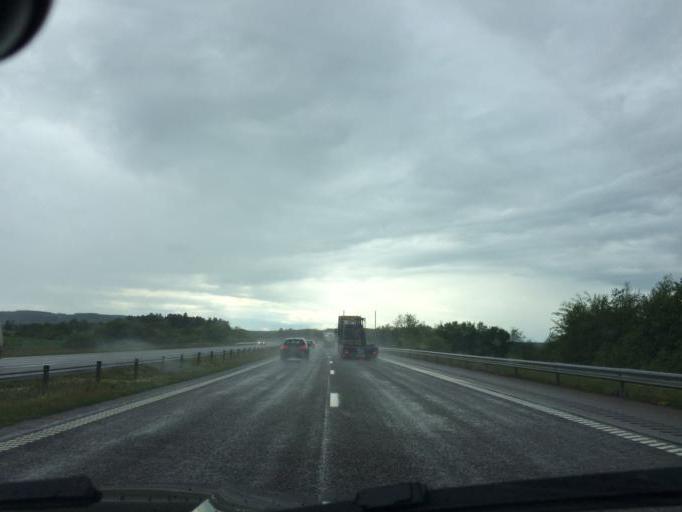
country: SE
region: Halland
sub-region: Halmstads Kommun
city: Getinge
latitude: 56.8028
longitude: 12.7619
